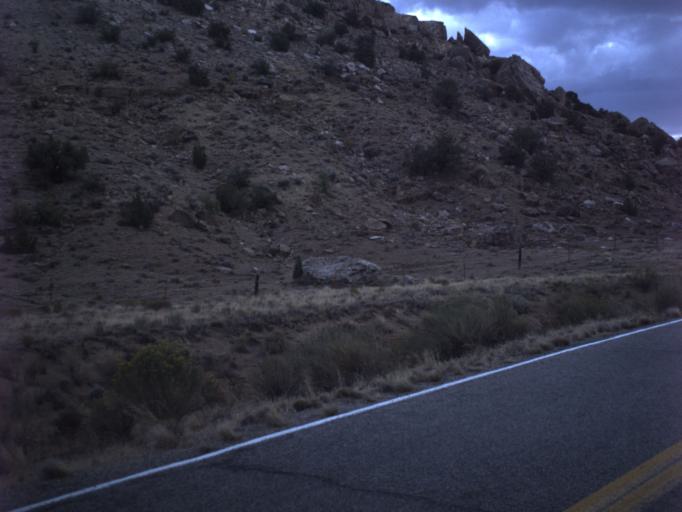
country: US
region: Utah
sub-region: San Juan County
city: Blanding
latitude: 37.4300
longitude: -109.4072
